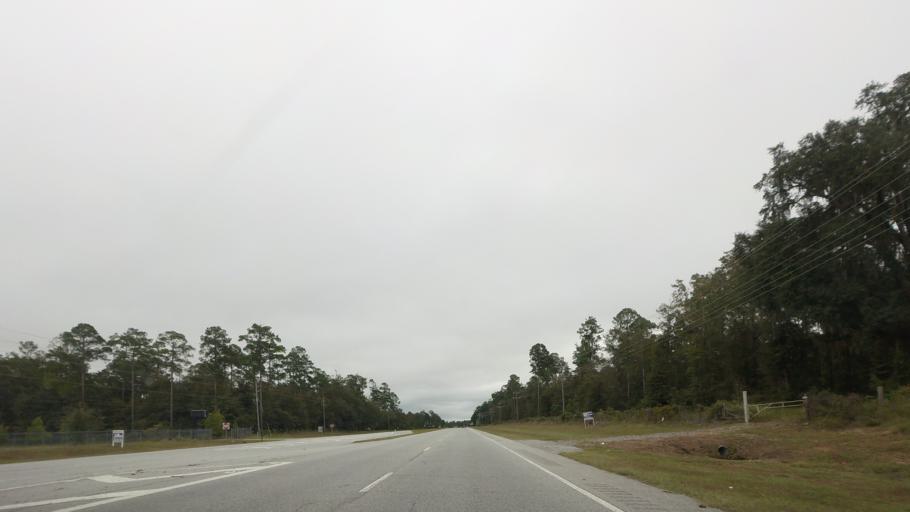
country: US
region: Georgia
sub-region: Lowndes County
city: Valdosta
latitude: 30.8787
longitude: -83.2413
